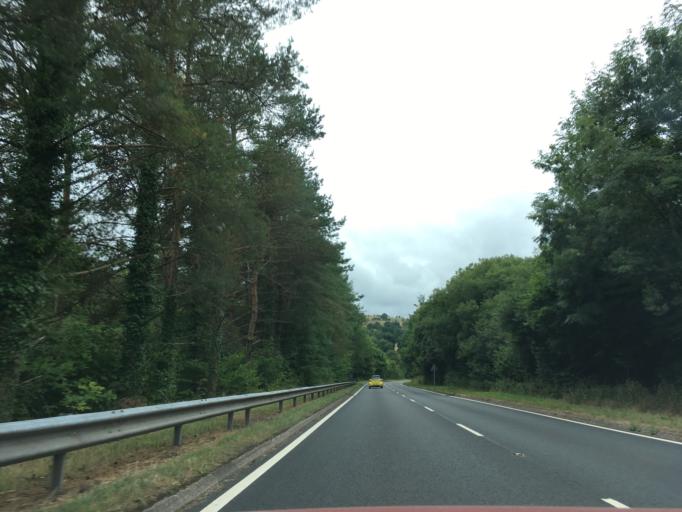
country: GB
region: Wales
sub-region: Sir Powys
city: Cray
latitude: 51.9596
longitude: -3.6614
